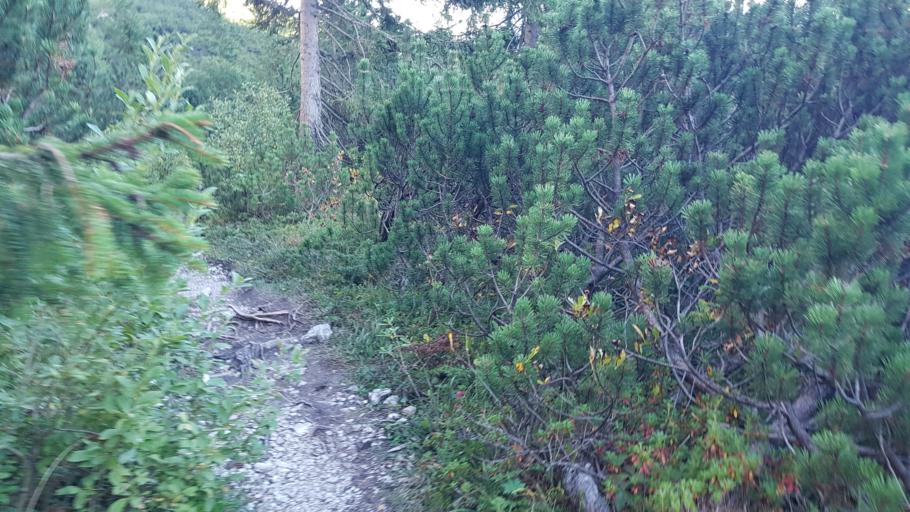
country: IT
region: Veneto
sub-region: Provincia di Belluno
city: La Valle Agordina
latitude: 46.3269
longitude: 12.0598
